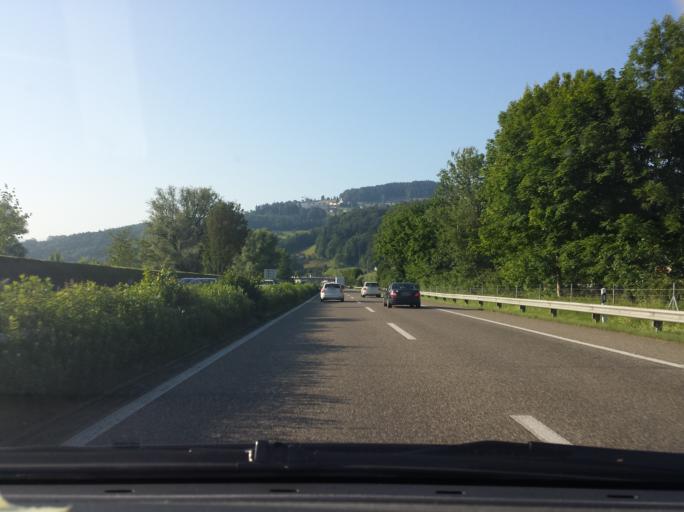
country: CH
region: Saint Gallen
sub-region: Wahlkreis Rheintal
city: Rheineck
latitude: 47.4692
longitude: 9.5901
